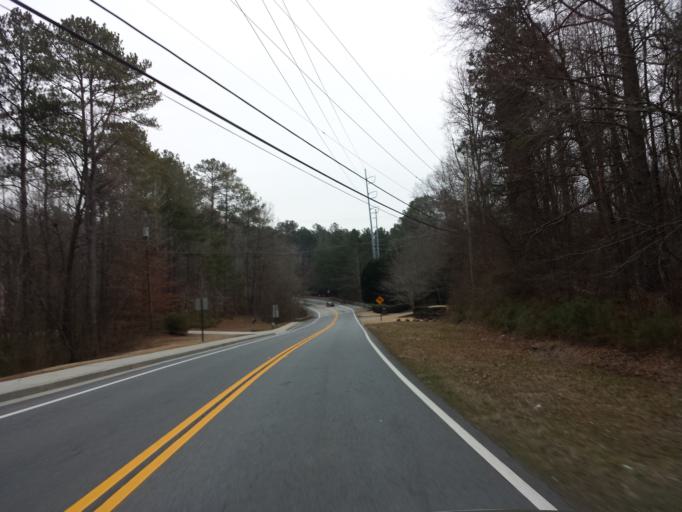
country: US
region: Georgia
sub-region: Fulton County
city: Roswell
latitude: 34.0162
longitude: -84.4007
